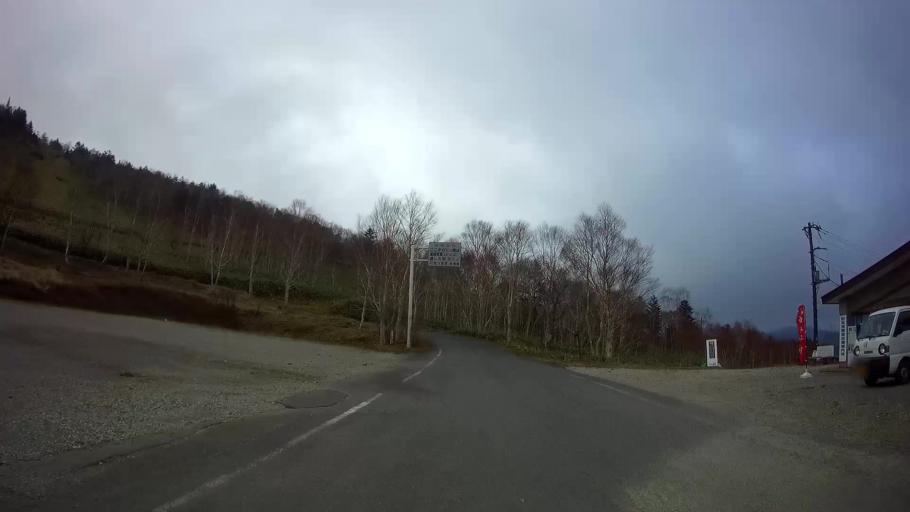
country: JP
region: Gunma
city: Nakanojomachi
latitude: 36.7198
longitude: 138.6428
